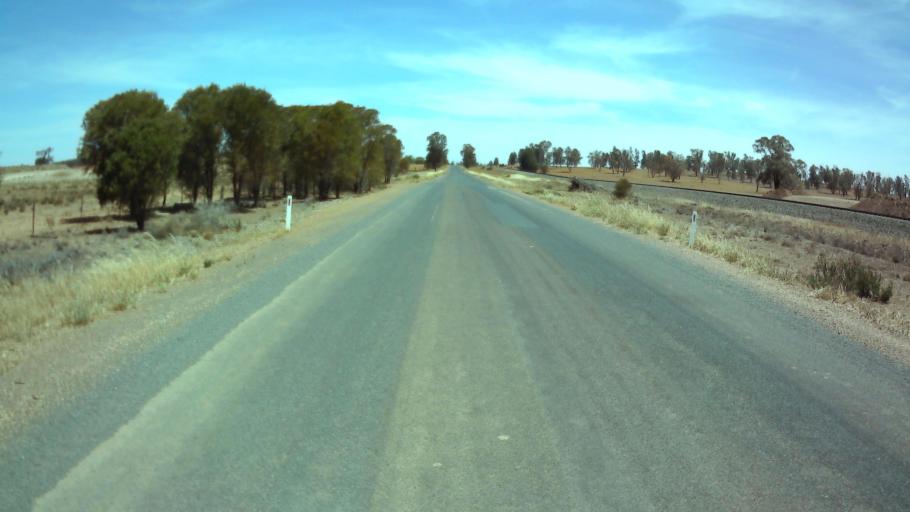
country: AU
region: New South Wales
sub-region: Weddin
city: Grenfell
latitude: -33.7666
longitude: 147.7587
